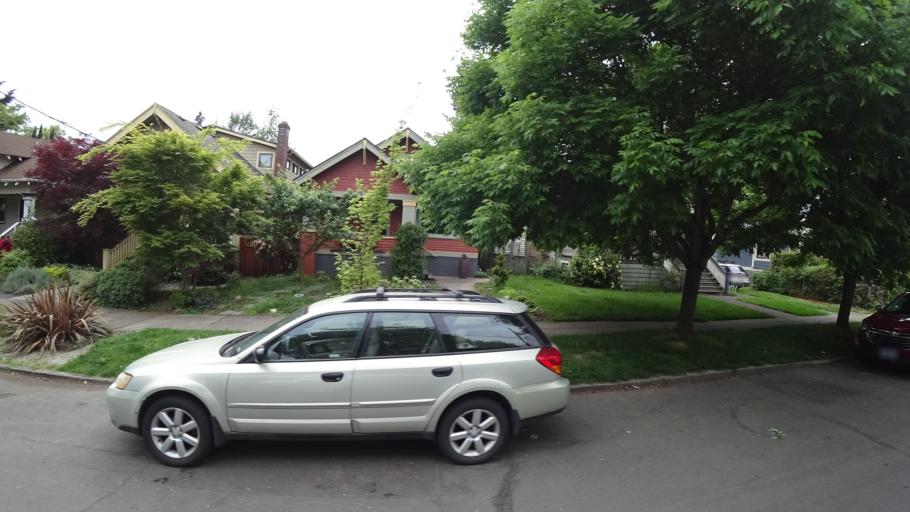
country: US
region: Oregon
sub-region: Multnomah County
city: Lents
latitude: 45.5105
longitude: -122.6131
